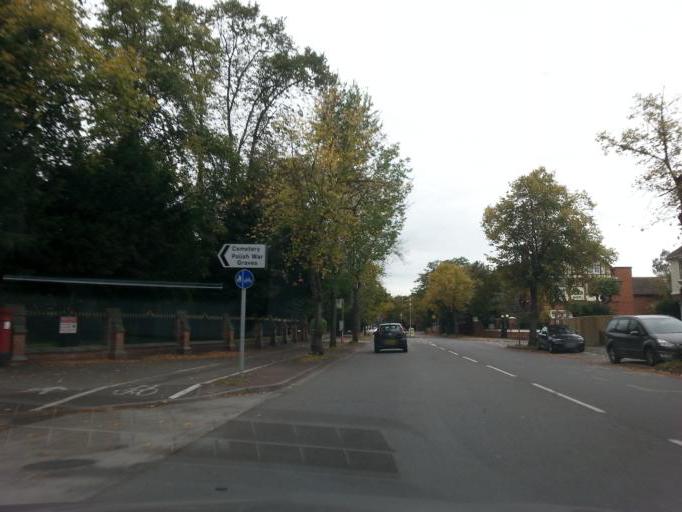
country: GB
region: England
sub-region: Nottinghamshire
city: Newark on Trent
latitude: 53.0693
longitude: -0.7987
